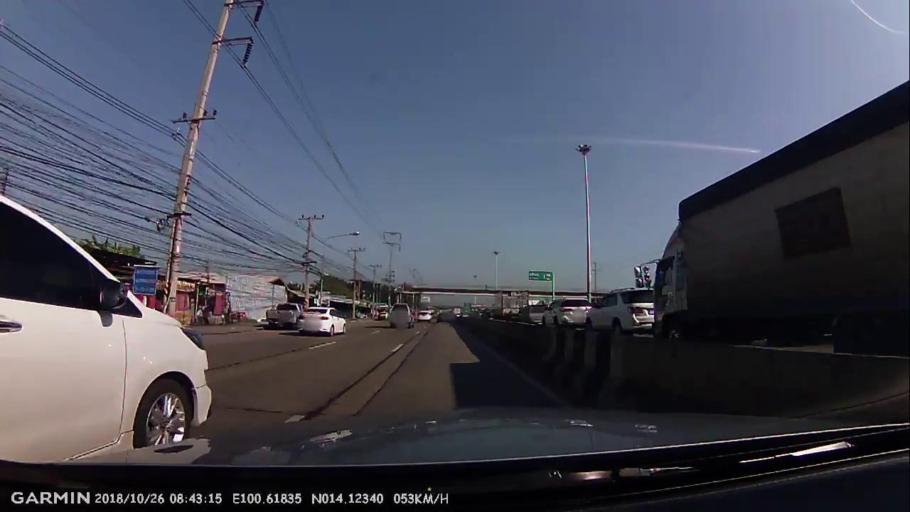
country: TH
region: Pathum Thani
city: Khlong Luang
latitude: 14.1236
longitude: 100.6183
